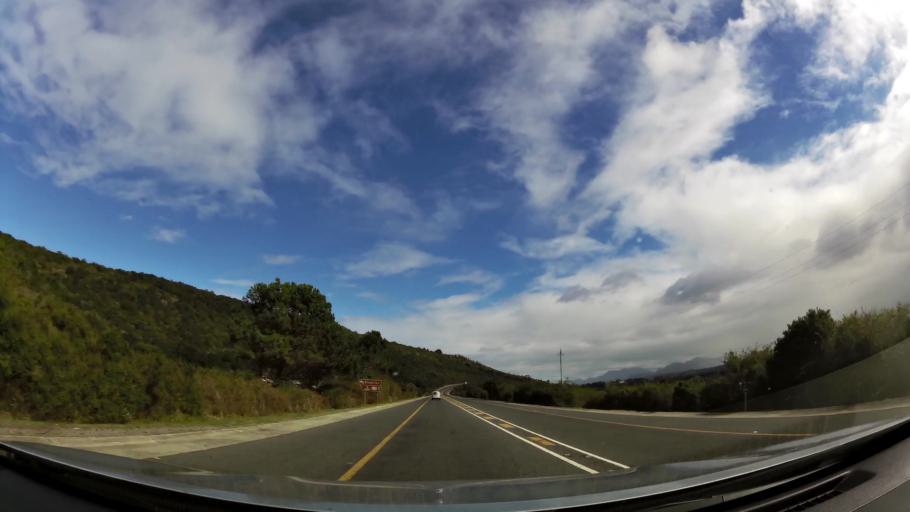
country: ZA
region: Western Cape
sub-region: Eden District Municipality
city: Knysna
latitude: -34.0094
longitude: 22.7579
